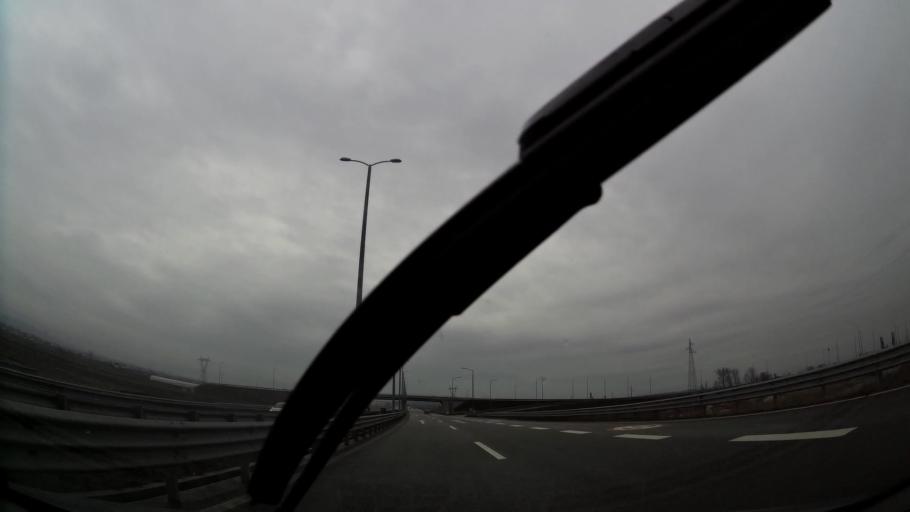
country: XK
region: Pristina
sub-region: Lipjan
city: Lipljan
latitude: 42.4640
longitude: 21.1782
